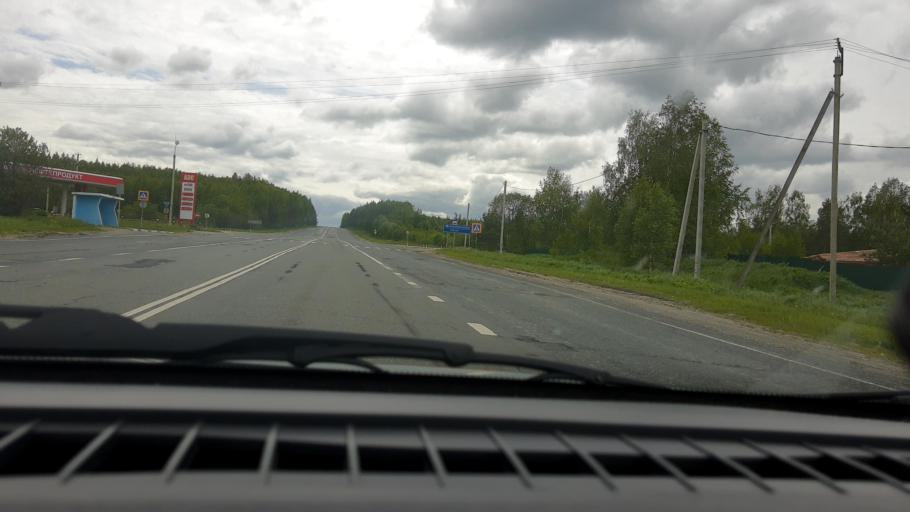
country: RU
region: Nizjnij Novgorod
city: Vladimirskoye
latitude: 56.9729
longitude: 45.1124
